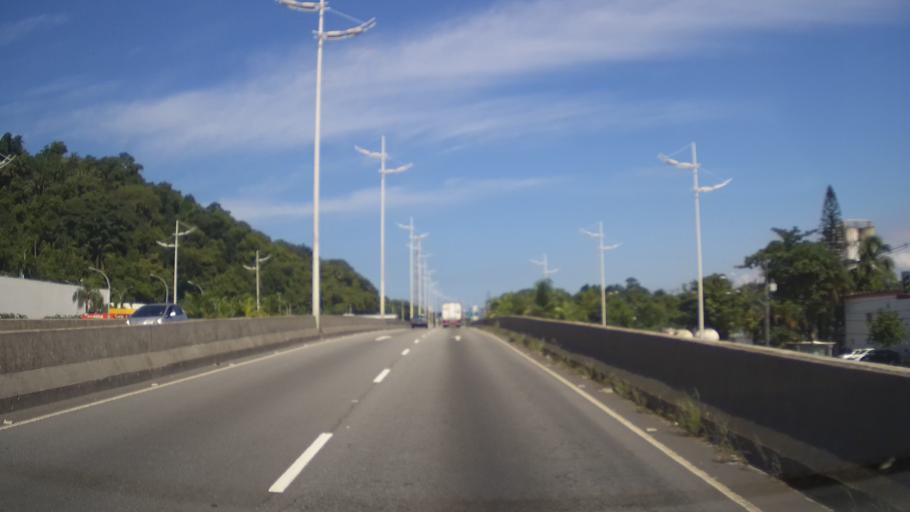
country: BR
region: Sao Paulo
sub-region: Praia Grande
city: Praia Grande
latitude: -23.9956
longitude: -46.4082
